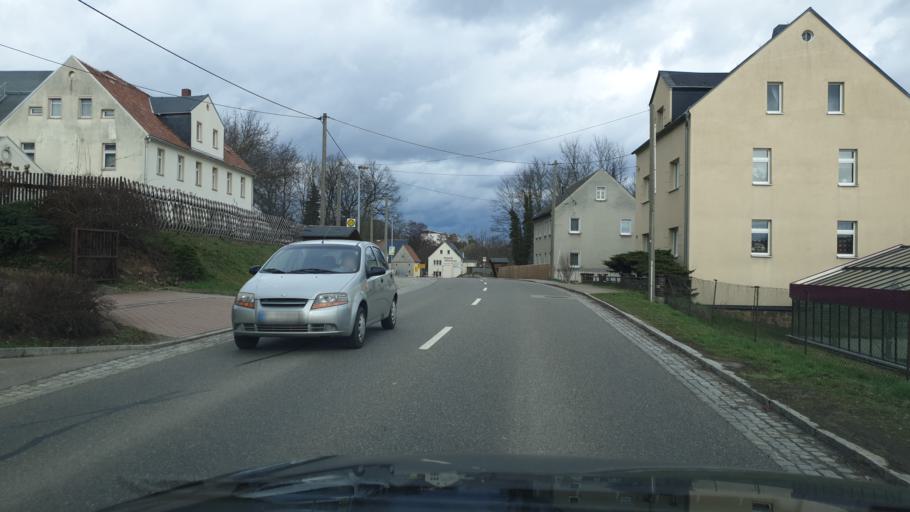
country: DE
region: Saxony
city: Claussnitz
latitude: 50.9350
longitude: 12.8808
